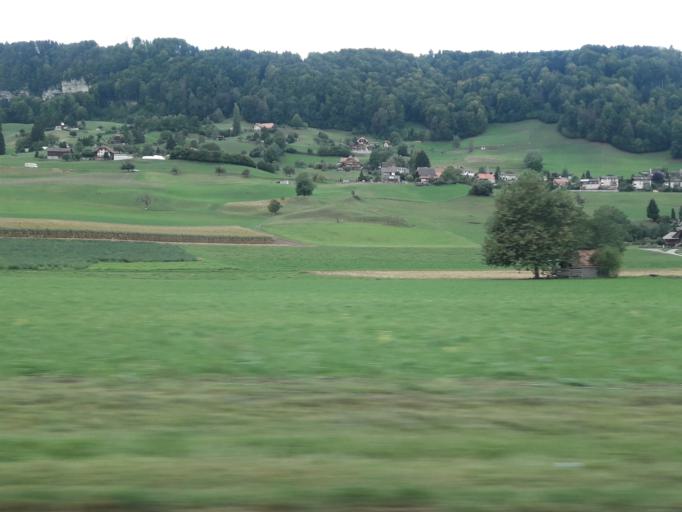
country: CH
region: Bern
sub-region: Bern-Mittelland District
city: Toffen
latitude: 46.8490
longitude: 7.4982
